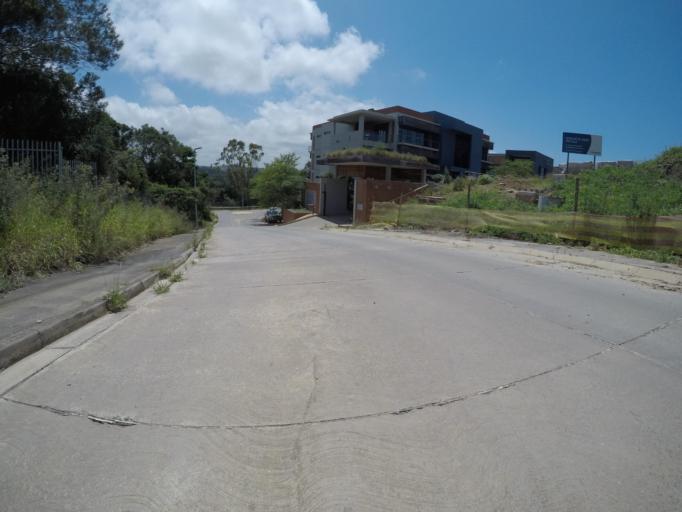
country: ZA
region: Eastern Cape
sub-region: Buffalo City Metropolitan Municipality
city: East London
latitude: -32.9483
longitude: 27.9407
